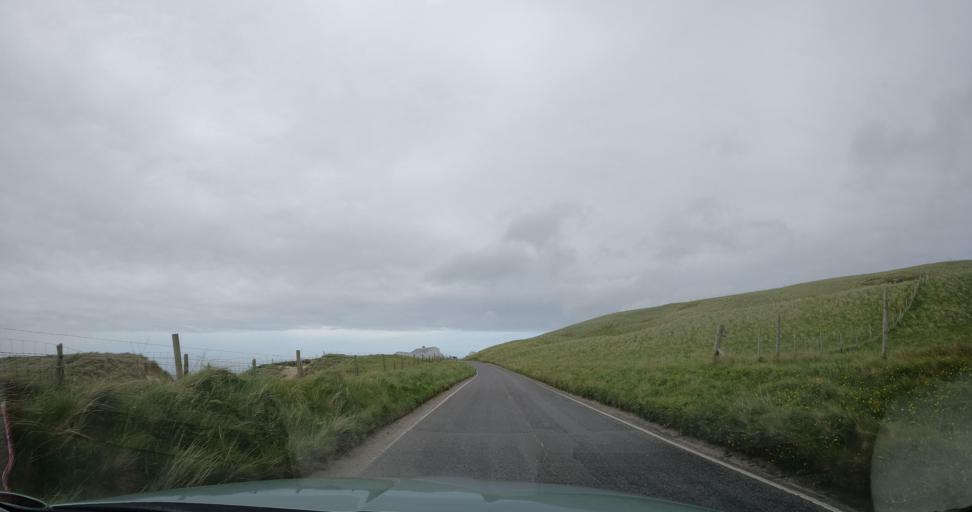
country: GB
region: Scotland
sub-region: Eilean Siar
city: Barra
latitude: 56.9737
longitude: -7.5165
